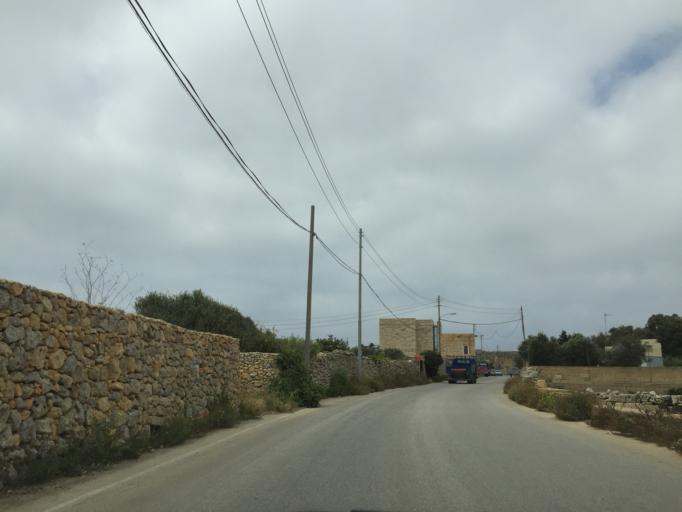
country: MT
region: Dingli
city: Dingli
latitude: 35.8810
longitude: 14.3688
